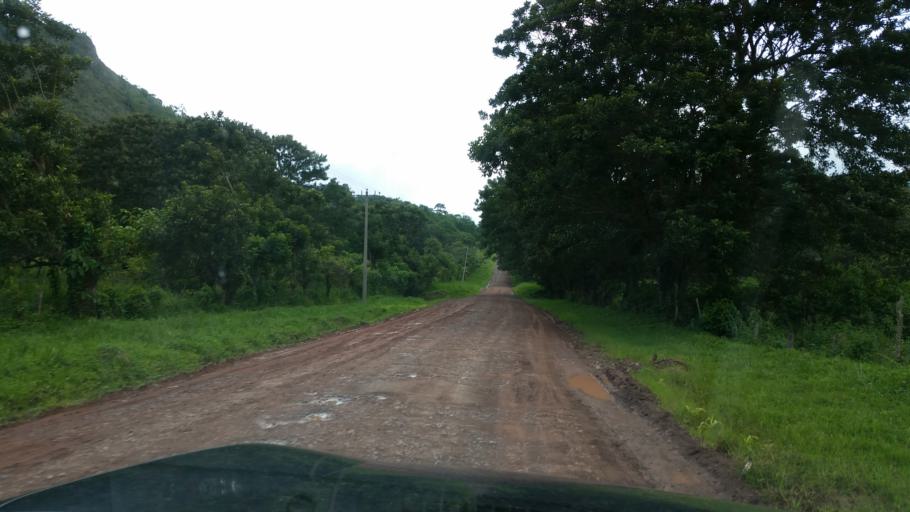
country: NI
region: Jinotega
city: Jinotega
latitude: 13.2217
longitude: -85.7309
